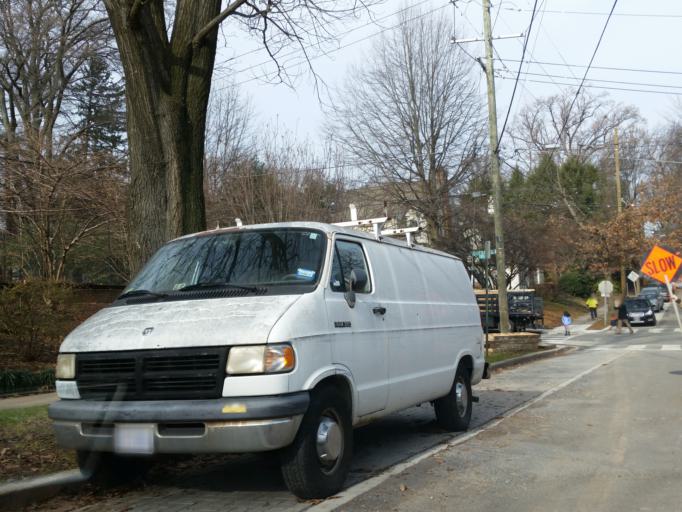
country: US
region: Maryland
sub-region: Montgomery County
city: Chevy Chase
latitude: 38.9684
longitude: -77.0664
